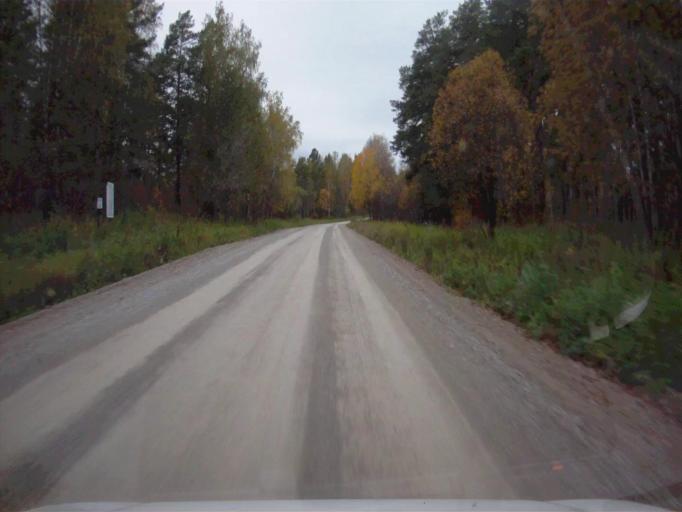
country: RU
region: Chelyabinsk
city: Nyazepetrovsk
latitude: 56.0623
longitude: 59.4469
